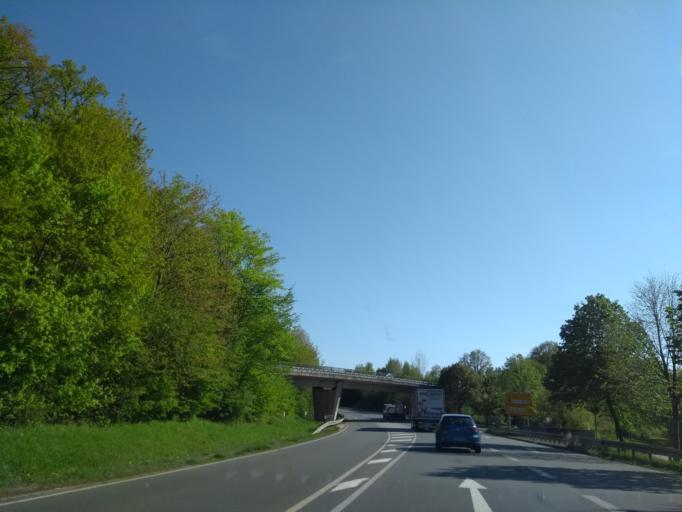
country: DE
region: Hesse
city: Frankenberg
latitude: 51.0713
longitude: 8.8133
